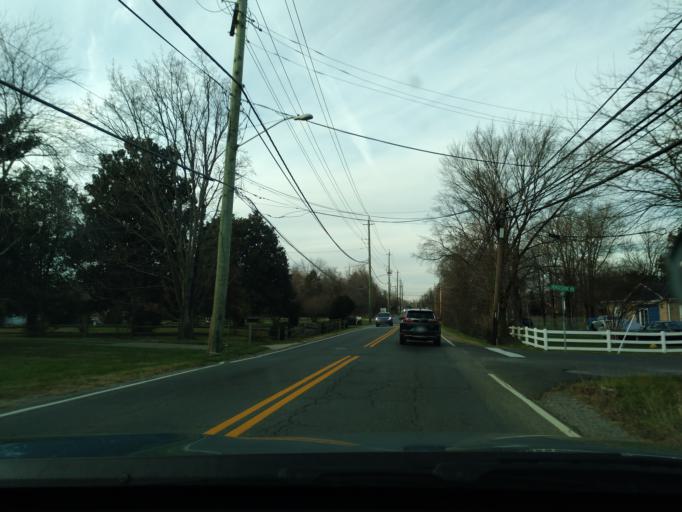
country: US
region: Maryland
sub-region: Prince George's County
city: Clinton
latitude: 38.7620
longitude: -76.8966
